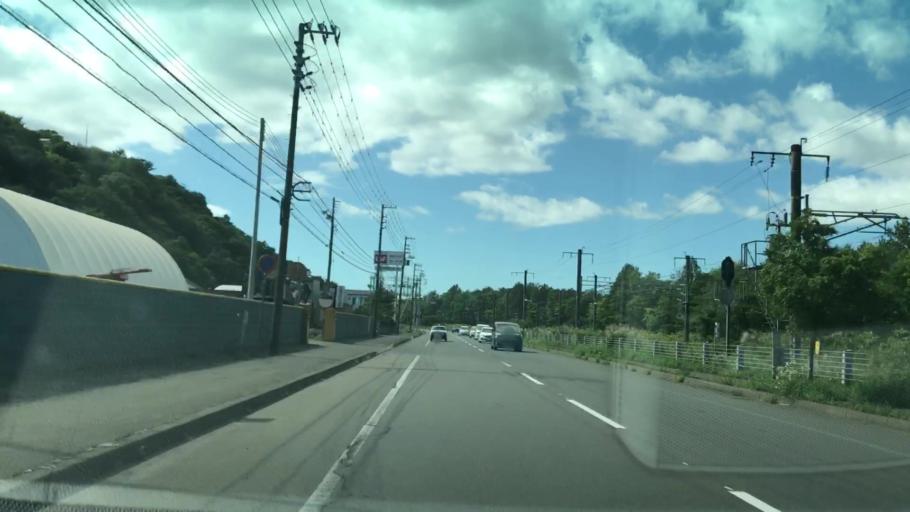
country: JP
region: Hokkaido
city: Muroran
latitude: 42.3345
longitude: 140.9988
